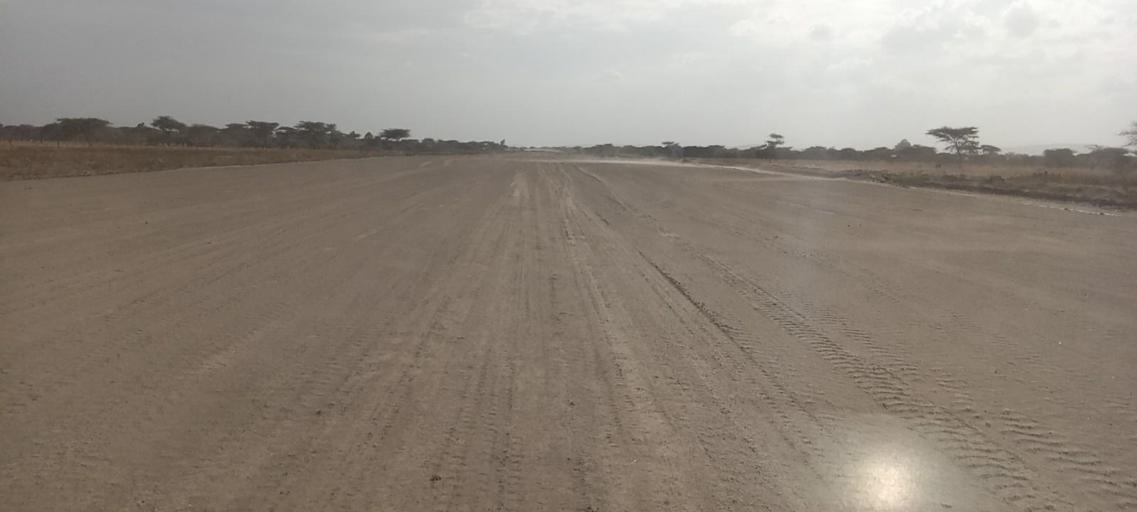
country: ET
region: Oromiya
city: Ziway
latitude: 7.9096
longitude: 38.6807
